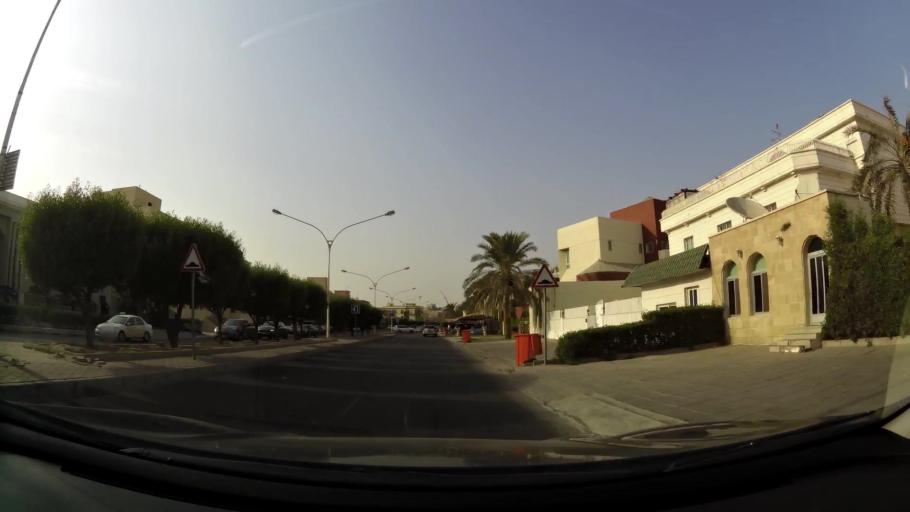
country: KW
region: Muhafazat Hawalli
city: Hawalli
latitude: 29.3157
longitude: 48.0032
